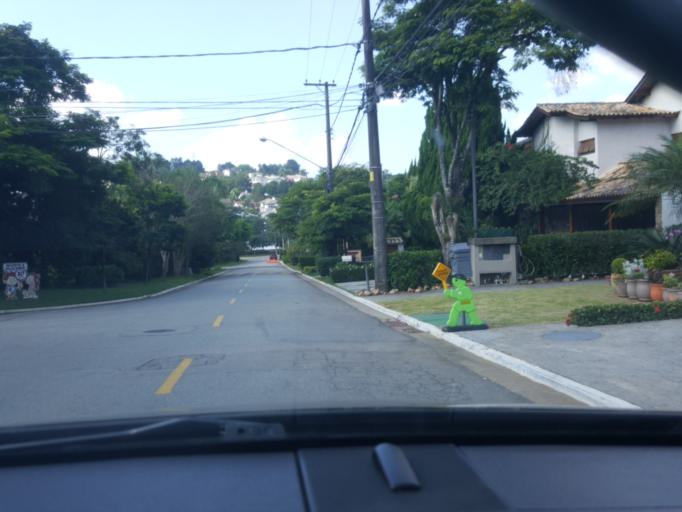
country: BR
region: Sao Paulo
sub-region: Carapicuiba
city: Carapicuiba
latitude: -23.4855
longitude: -46.8374
